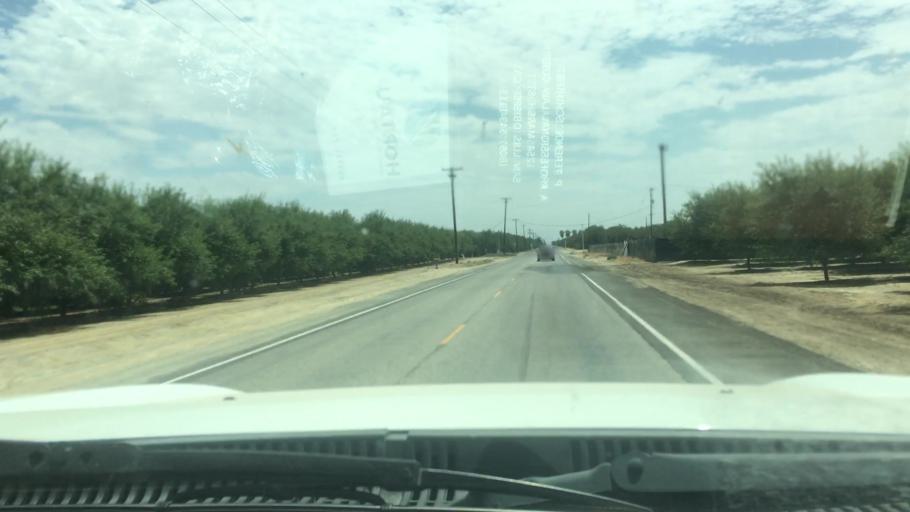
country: US
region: California
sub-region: Kern County
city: Wasco
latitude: 35.5580
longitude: -119.3517
